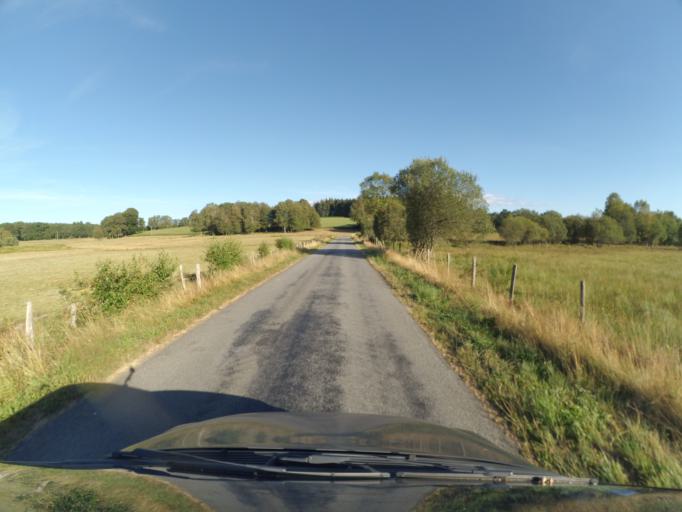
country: FR
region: Limousin
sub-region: Departement de la Creuse
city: Banize
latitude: 45.7208
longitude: 2.0422
